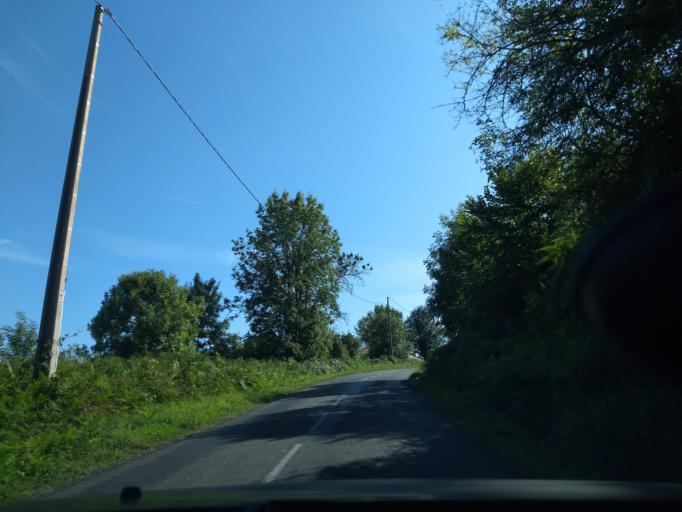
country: FR
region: Aquitaine
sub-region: Departement des Pyrenees-Atlantiques
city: Soumoulou
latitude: 43.2954
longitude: -0.1586
